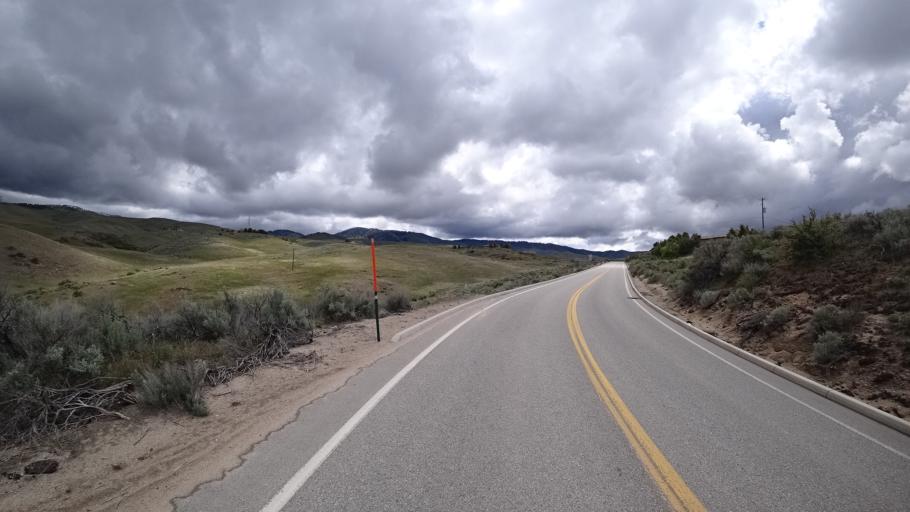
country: US
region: Idaho
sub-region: Ada County
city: Boise
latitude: 43.6948
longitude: -116.1780
